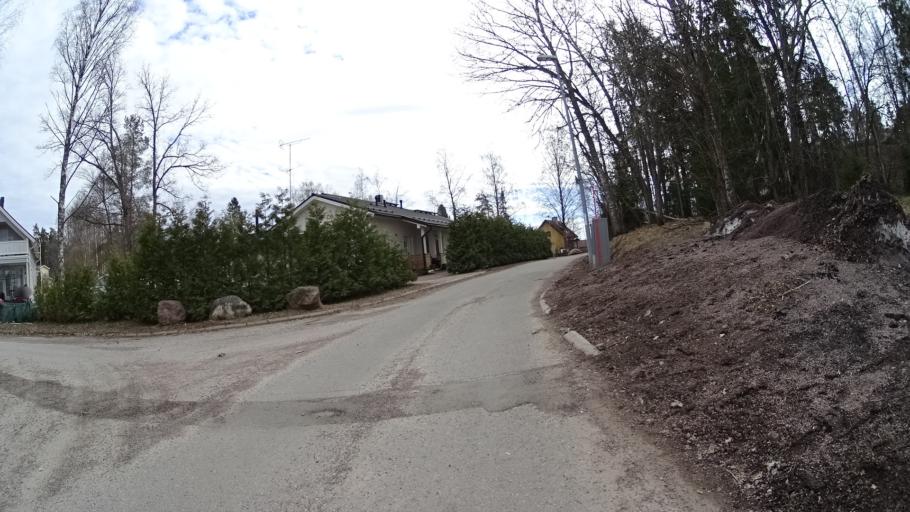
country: FI
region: Uusimaa
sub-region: Helsinki
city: Kauniainen
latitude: 60.2691
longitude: 24.7460
